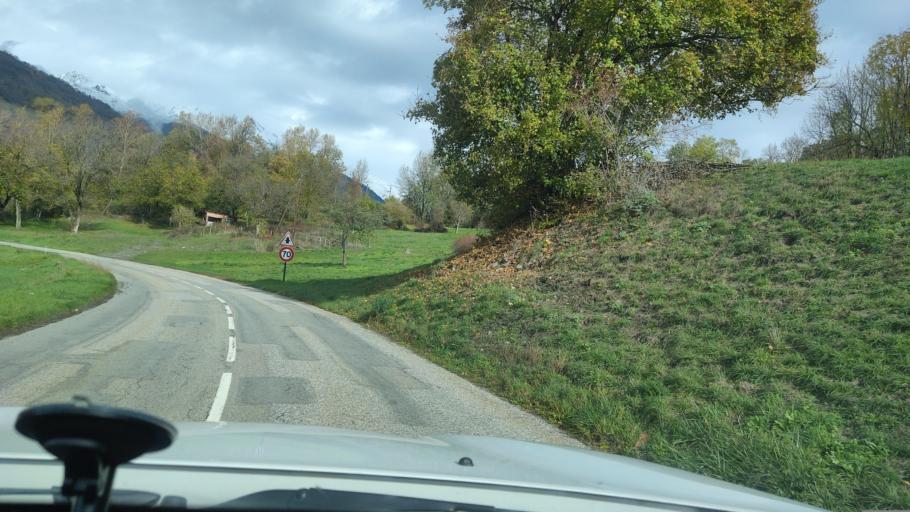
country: FR
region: Rhone-Alpes
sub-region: Departement de la Savoie
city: Bourg-Saint-Maurice
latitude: 45.5756
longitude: 6.7446
